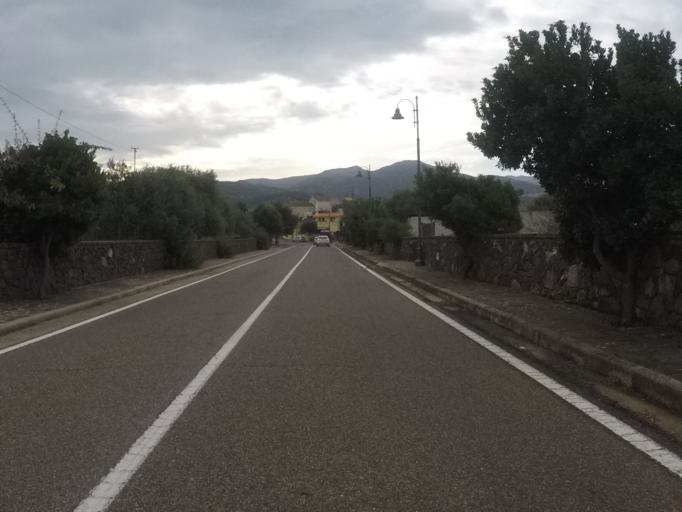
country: IT
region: Sardinia
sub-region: Provincia di Oristano
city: Sennariolo
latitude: 40.2138
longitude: 8.5541
